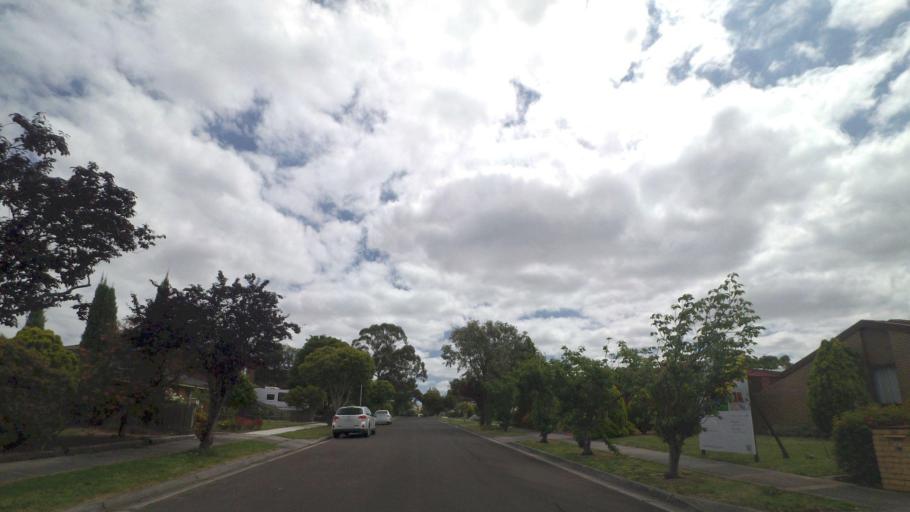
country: AU
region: Victoria
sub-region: Knox
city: Wantirna
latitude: -37.8665
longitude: 145.2232
